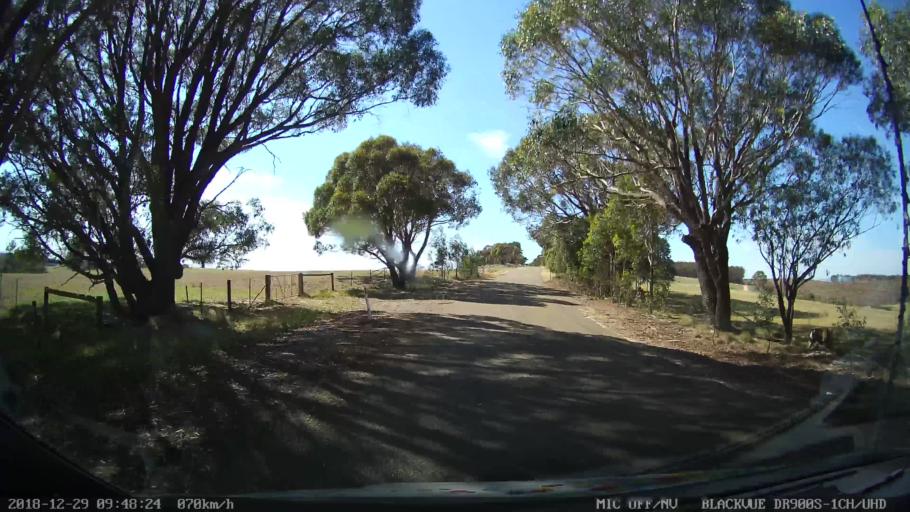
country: AU
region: New South Wales
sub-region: Upper Lachlan Shire
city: Crookwell
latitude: -34.7156
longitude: 149.4554
